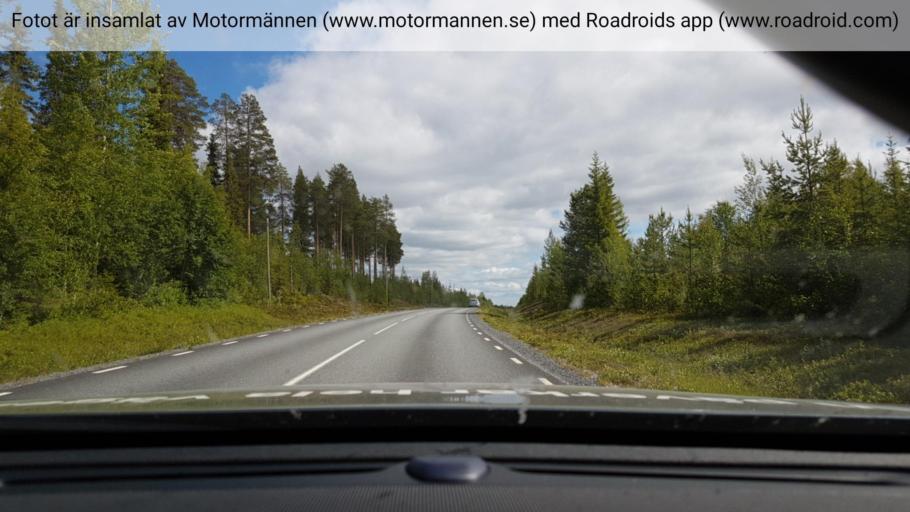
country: SE
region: Vaesterbotten
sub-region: Sorsele Kommun
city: Sorsele
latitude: 65.6608
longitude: 17.4210
